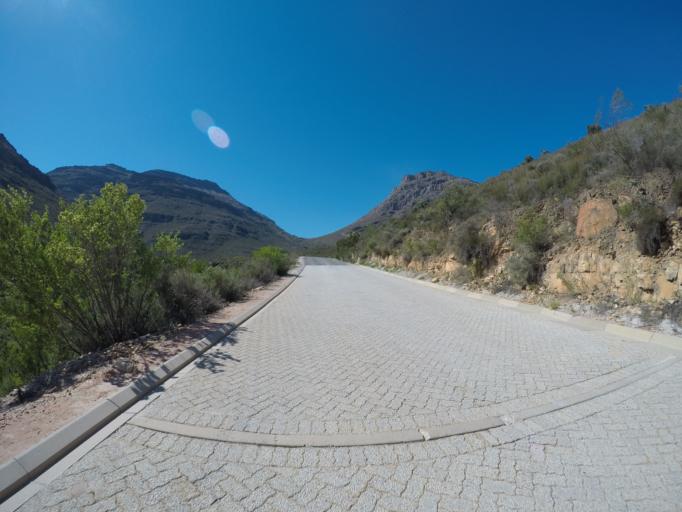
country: ZA
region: Western Cape
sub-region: West Coast District Municipality
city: Clanwilliam
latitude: -32.3939
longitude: 19.0844
